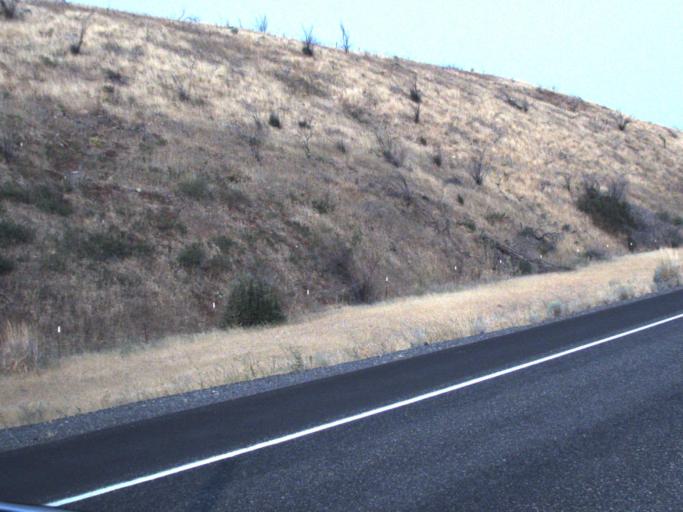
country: US
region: Washington
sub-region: Kittitas County
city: Ellensburg
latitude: 47.0843
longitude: -120.6435
